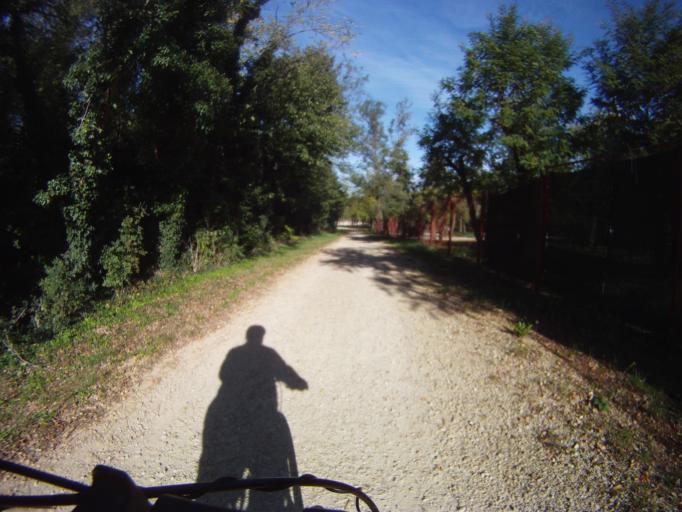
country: HR
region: Istarska
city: Novigrad
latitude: 45.3391
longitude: 13.5448
